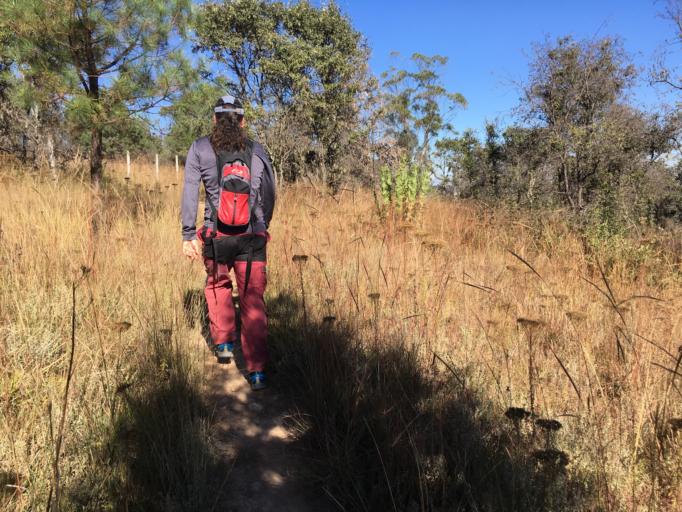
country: MX
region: Michoacan
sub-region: Morelia
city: Montana Monarca (Punta Altozano)
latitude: 19.6652
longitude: -101.1452
